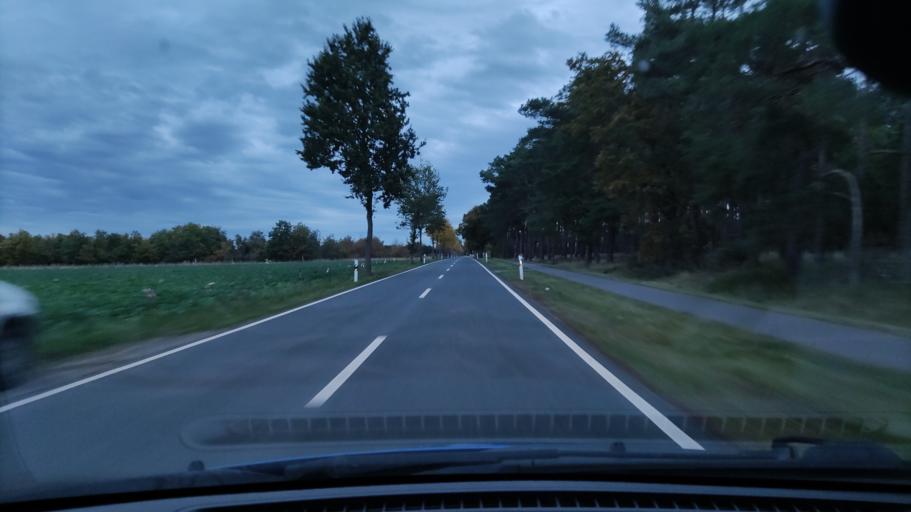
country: DE
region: Lower Saxony
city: Gorleben
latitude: 53.0608
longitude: 11.3973
